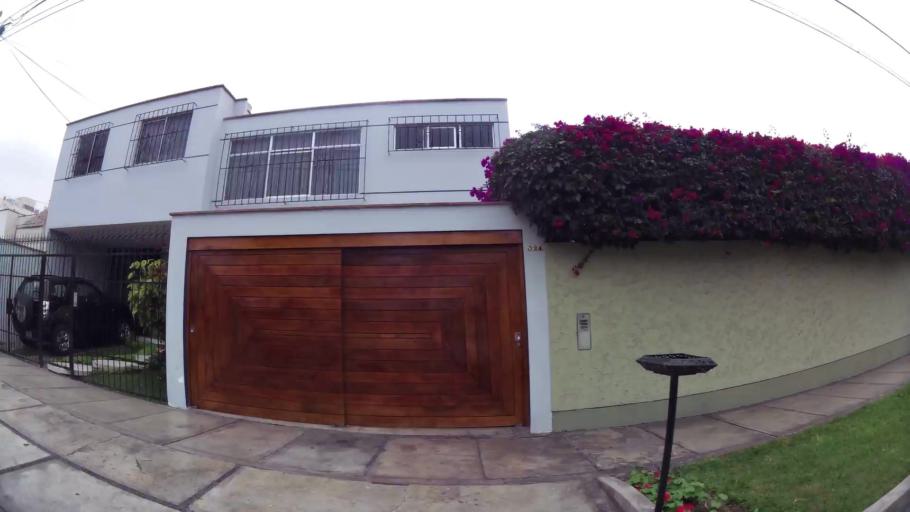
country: PE
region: Lima
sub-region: Lima
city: Surco
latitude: -12.1218
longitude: -77.0089
